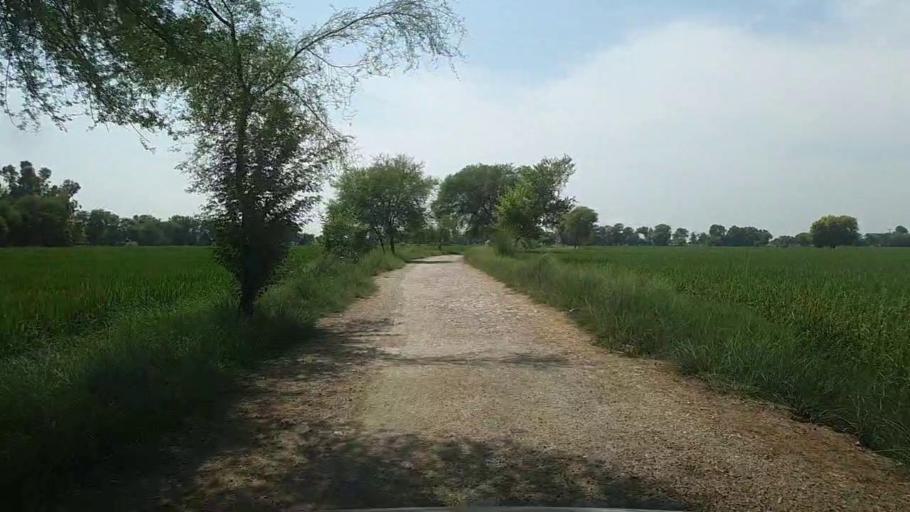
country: PK
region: Sindh
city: Kandhkot
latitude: 28.3109
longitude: 69.1986
